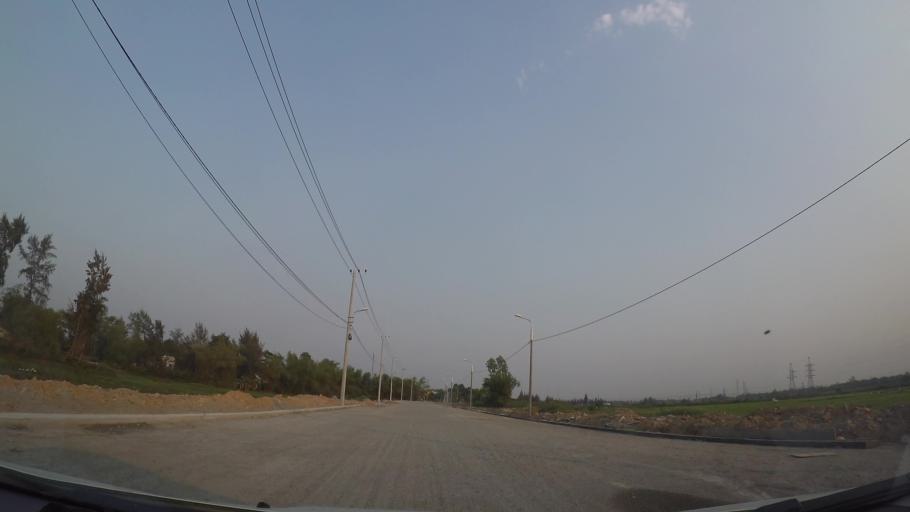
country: VN
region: Da Nang
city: Ngu Hanh Son
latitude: 15.9560
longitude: 108.2373
